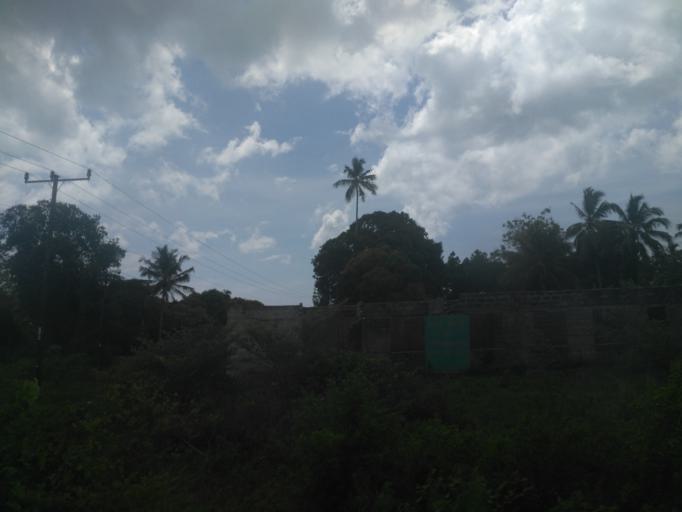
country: TZ
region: Zanzibar Urban/West
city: Zanzibar
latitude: -6.2654
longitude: 39.2635
